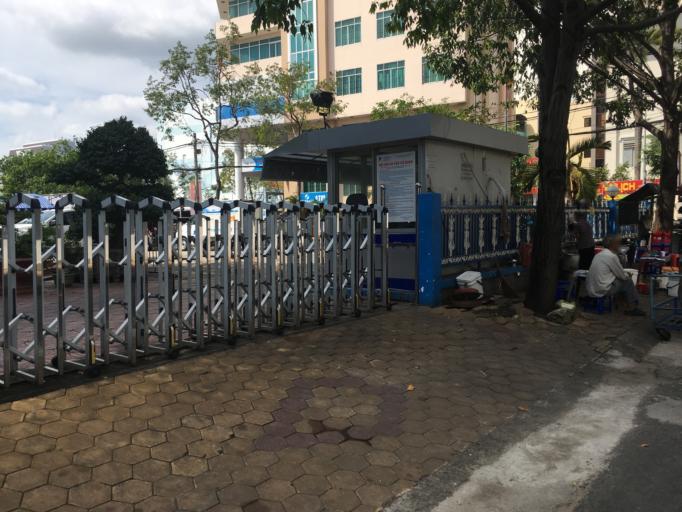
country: VN
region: Can Tho
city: Can Tho
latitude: 10.0347
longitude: 105.7874
